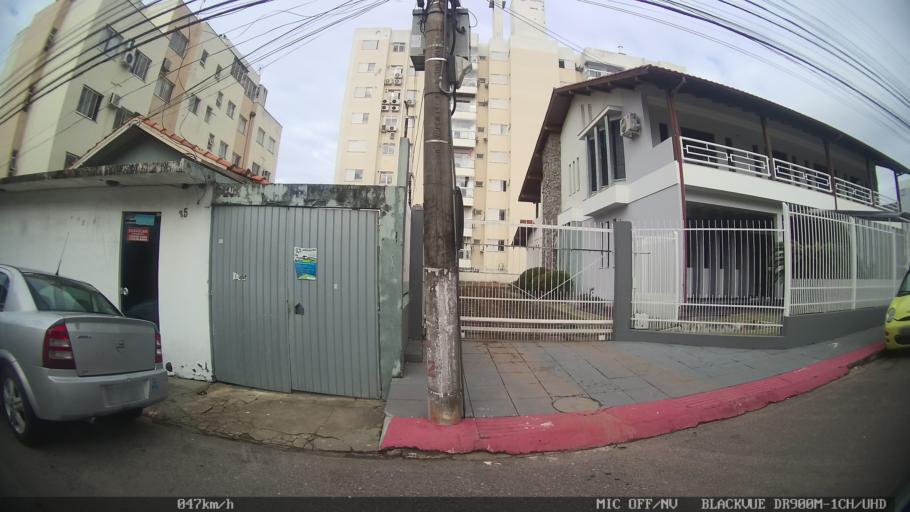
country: BR
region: Santa Catarina
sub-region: Sao Jose
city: Campinas
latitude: -27.5705
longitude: -48.6101
